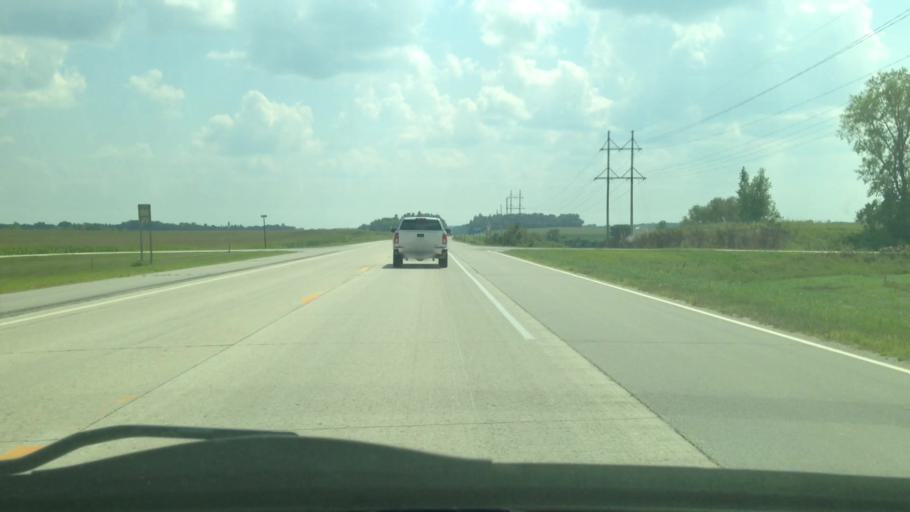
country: US
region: Minnesota
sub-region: Fillmore County
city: Spring Valley
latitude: 43.6464
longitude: -92.3894
